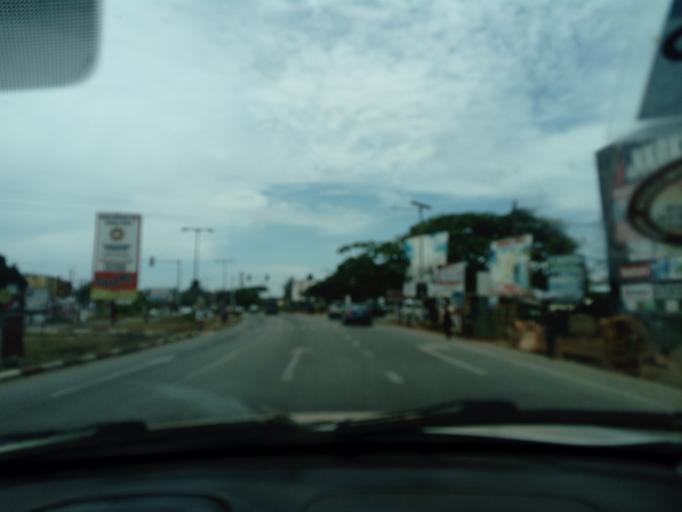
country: GH
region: Central
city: Cape Coast
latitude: 5.1233
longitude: -1.2691
